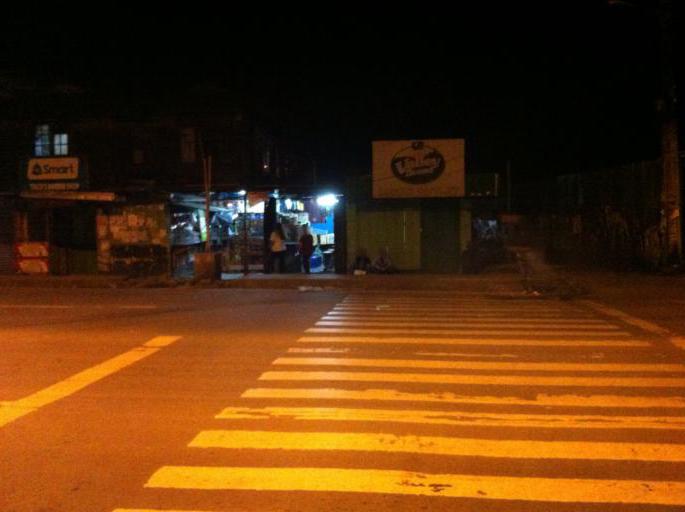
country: PH
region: Cordillera
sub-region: Province of Benguet
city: La Trinidad
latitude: 16.4552
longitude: 120.5893
